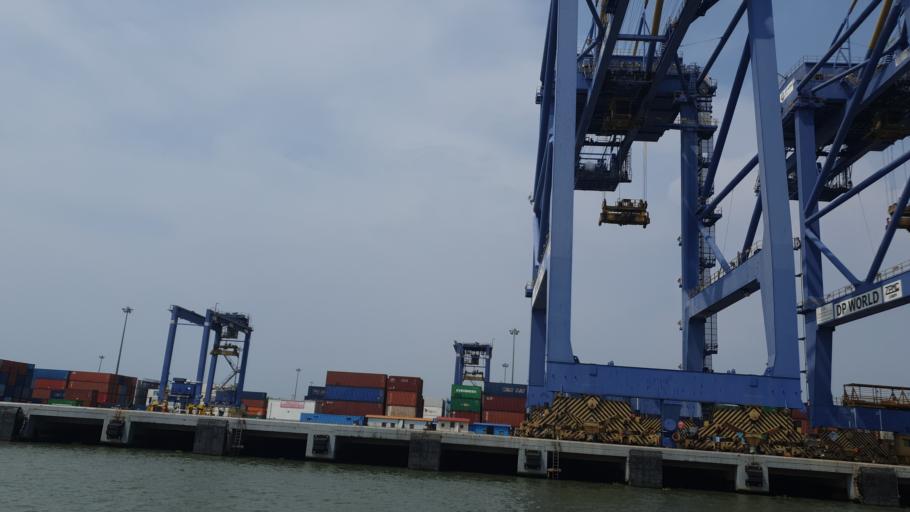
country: IN
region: Kerala
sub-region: Ernakulam
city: Cochin
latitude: 9.9774
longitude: 76.2529
